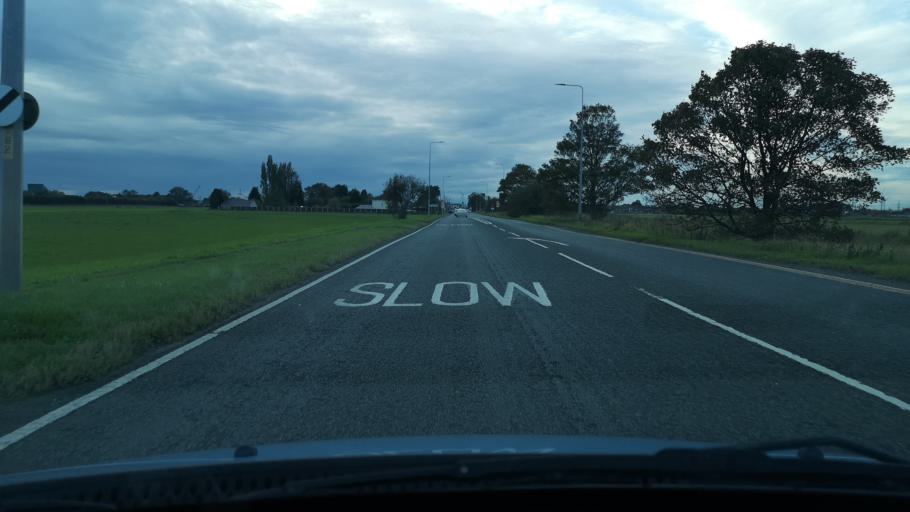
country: GB
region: England
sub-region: North Lincolnshire
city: Gunness
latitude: 53.5900
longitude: -0.7157
